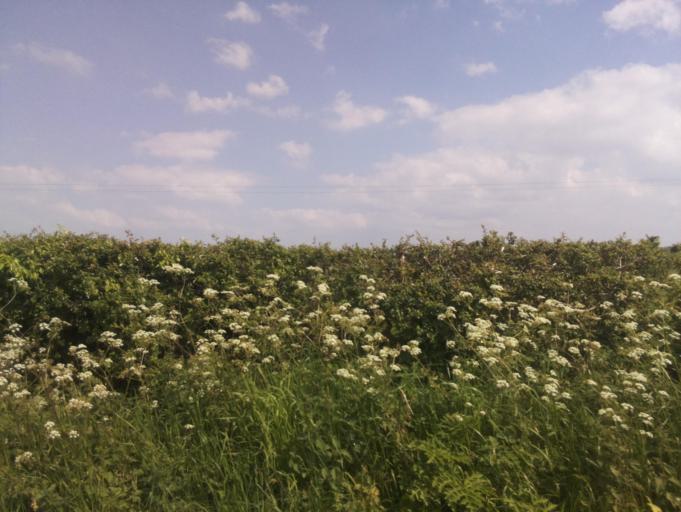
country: GB
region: England
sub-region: South Gloucestershire
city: Horton
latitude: 51.5737
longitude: -2.3222
